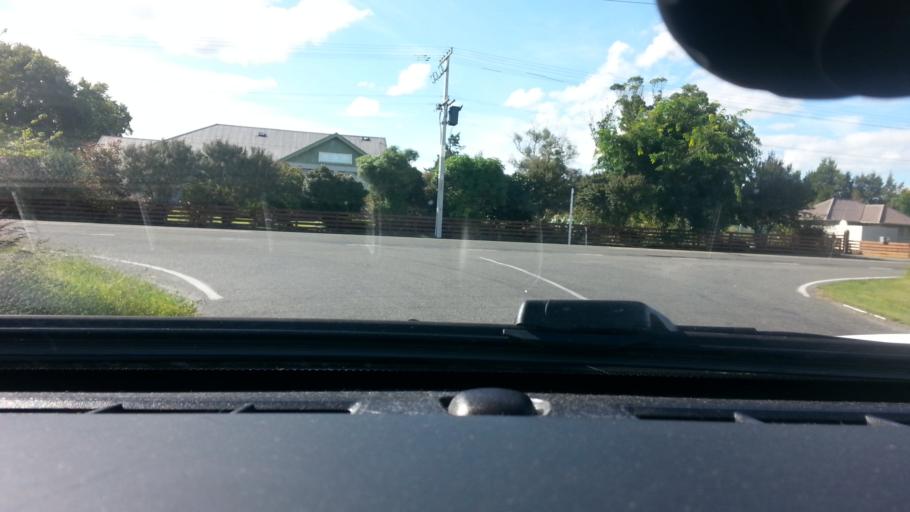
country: NZ
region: Wellington
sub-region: Masterton District
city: Masterton
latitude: -40.9504
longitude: 175.6945
